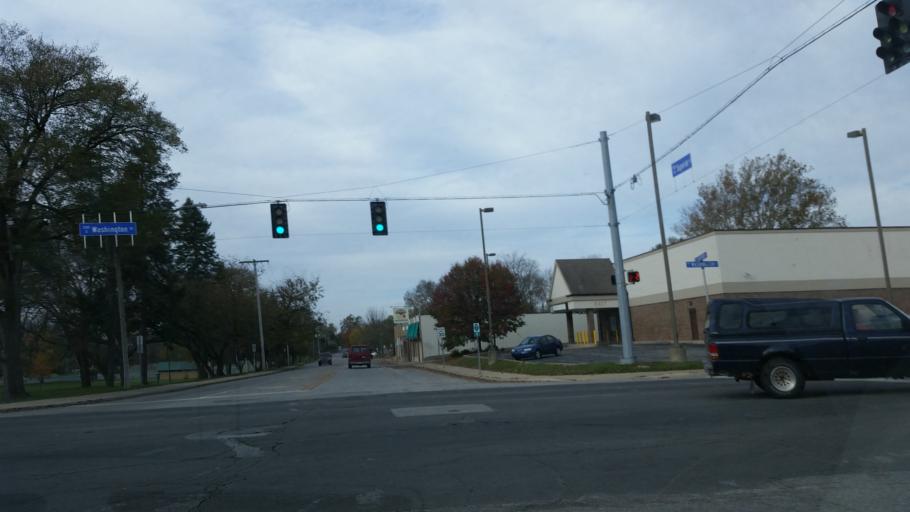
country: US
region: Indiana
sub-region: Howard County
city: Kokomo
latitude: 40.4856
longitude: -86.1335
